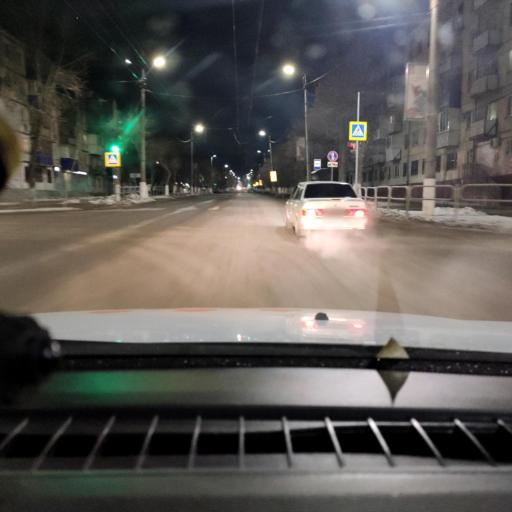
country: RU
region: Samara
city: Novokuybyshevsk
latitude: 53.0909
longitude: 49.9500
